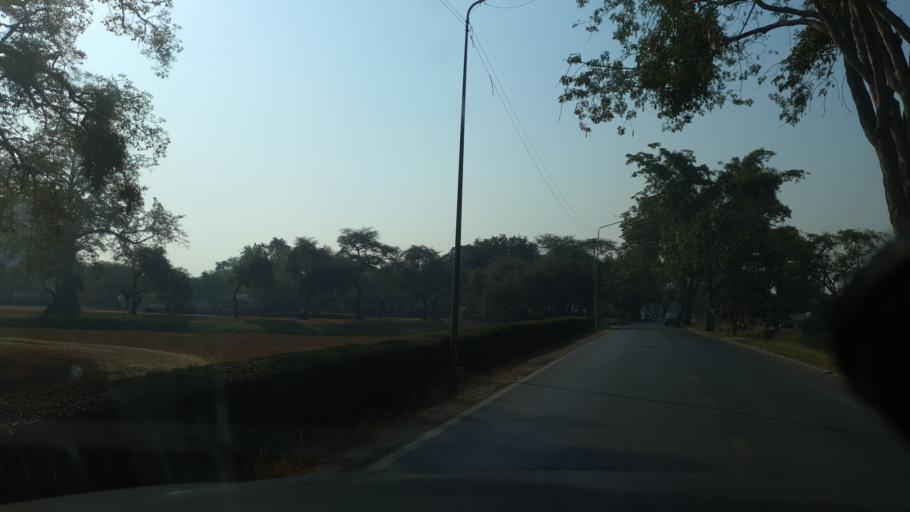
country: TH
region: Phra Nakhon Si Ayutthaya
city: Phra Nakhon Si Ayutthaya
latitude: 14.3565
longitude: 100.5557
